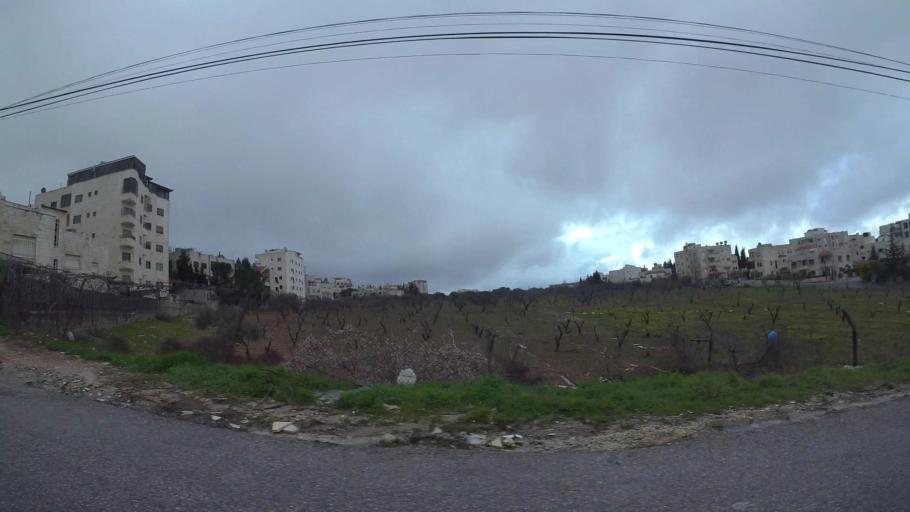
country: JO
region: Amman
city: Al Jubayhah
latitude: 32.0316
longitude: 35.8586
